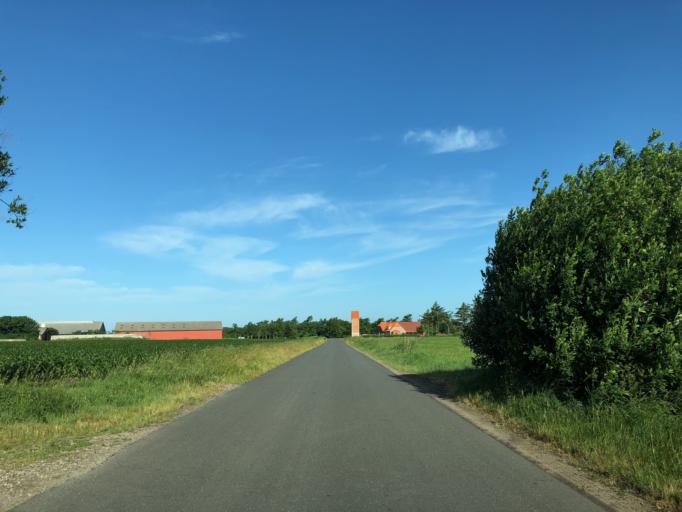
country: DK
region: Central Jutland
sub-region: Holstebro Kommune
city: Ulfborg
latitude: 56.3379
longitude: 8.2947
